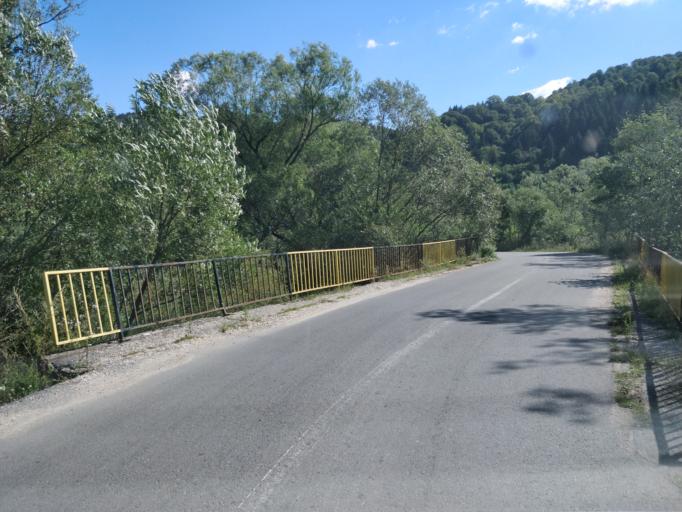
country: RO
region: Cluj
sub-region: Comuna Sacueu
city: Sacuieu
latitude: 46.8058
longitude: 22.8922
